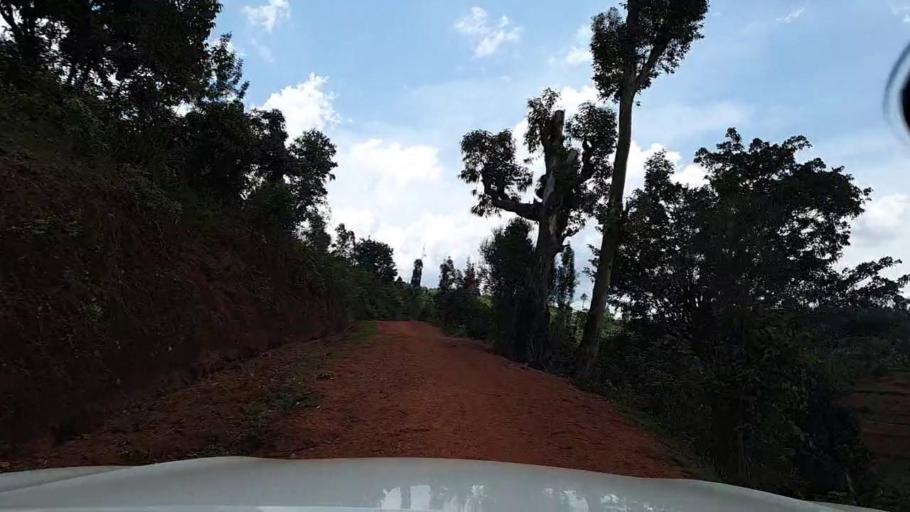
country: RW
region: Southern Province
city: Butare
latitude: -2.7481
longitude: 29.7623
